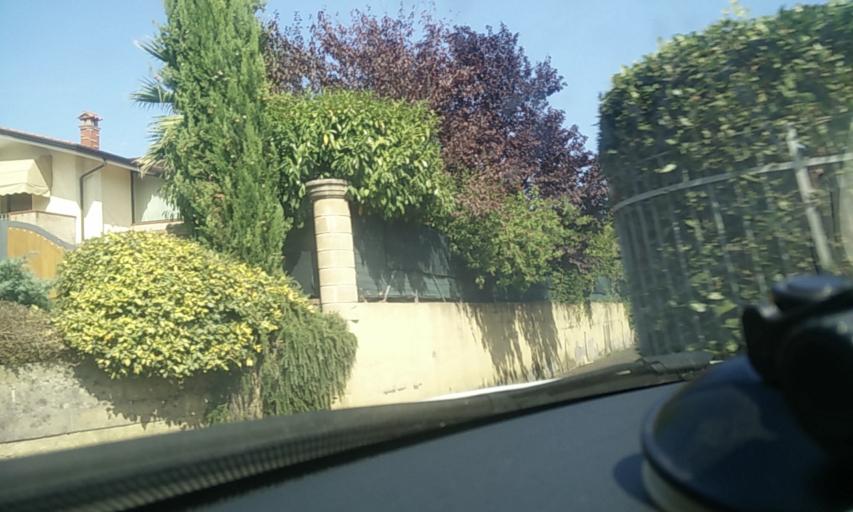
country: IT
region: Tuscany
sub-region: Provincia di Massa-Carrara
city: Massa
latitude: 44.0403
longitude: 10.1031
